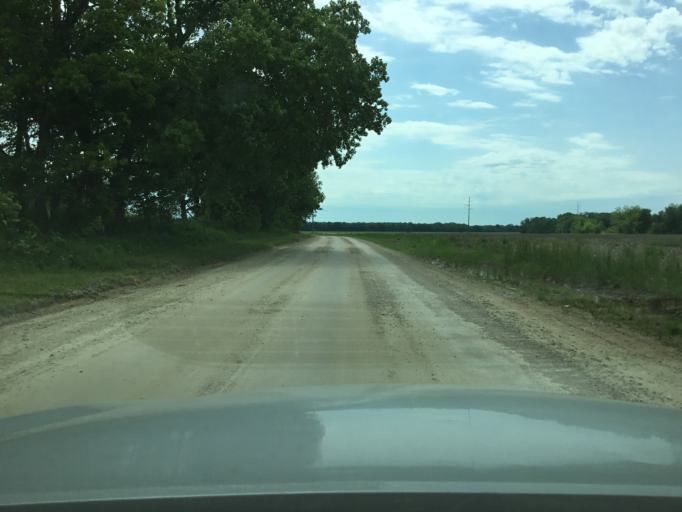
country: US
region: Kansas
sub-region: Montgomery County
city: Coffeyville
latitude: 37.0061
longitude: -95.6039
